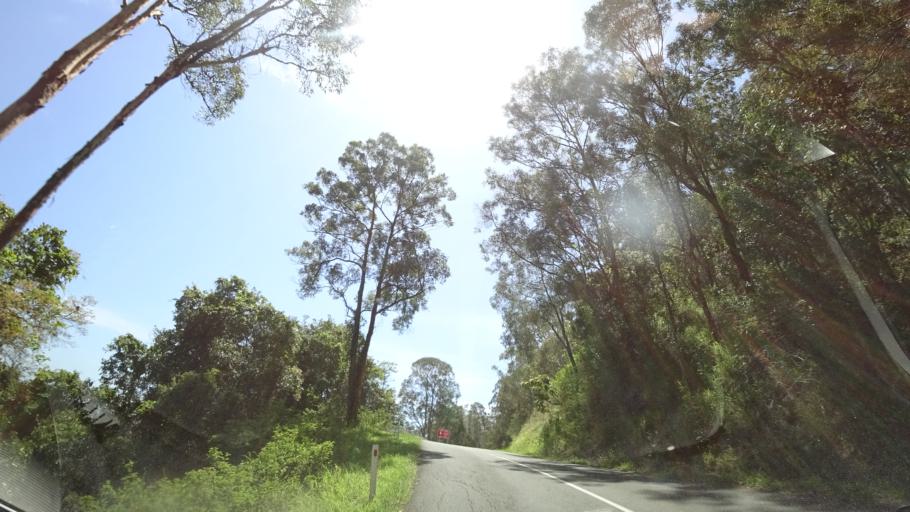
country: AU
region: Queensland
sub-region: Moreton Bay
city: Samford Valley
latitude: -27.4216
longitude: 152.8614
